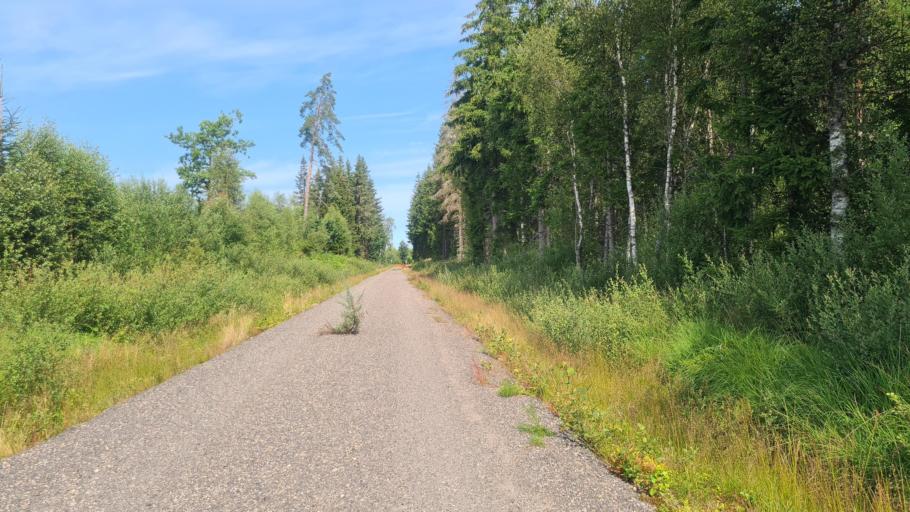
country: SE
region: Kronoberg
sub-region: Ljungby Kommun
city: Lagan
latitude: 56.9820
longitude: 13.9455
